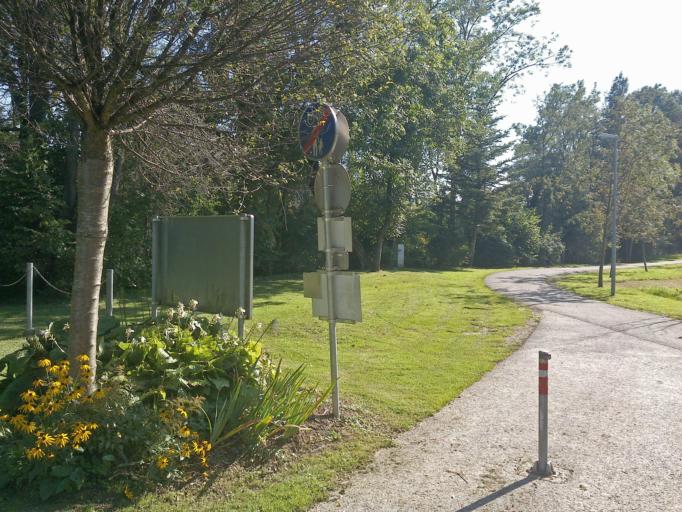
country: AT
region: Styria
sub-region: Politischer Bezirk Graz-Umgebung
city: Hausmannstatten
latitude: 46.9889
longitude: 15.5133
